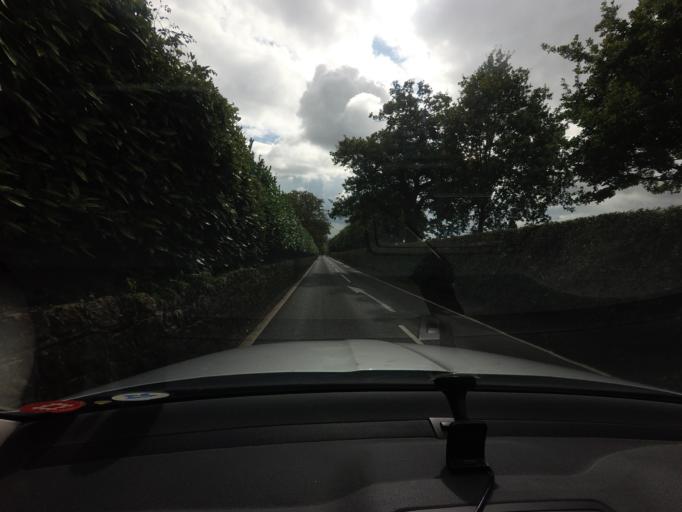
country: GB
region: England
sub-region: Kent
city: Borough Green
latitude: 51.2574
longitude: 0.2812
